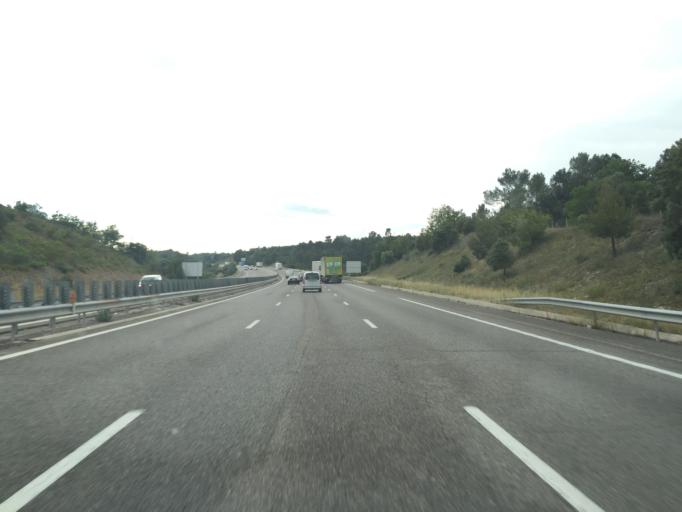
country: FR
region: Provence-Alpes-Cote d'Azur
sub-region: Departement du Var
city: Tourves
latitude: 43.4410
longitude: 5.9048
